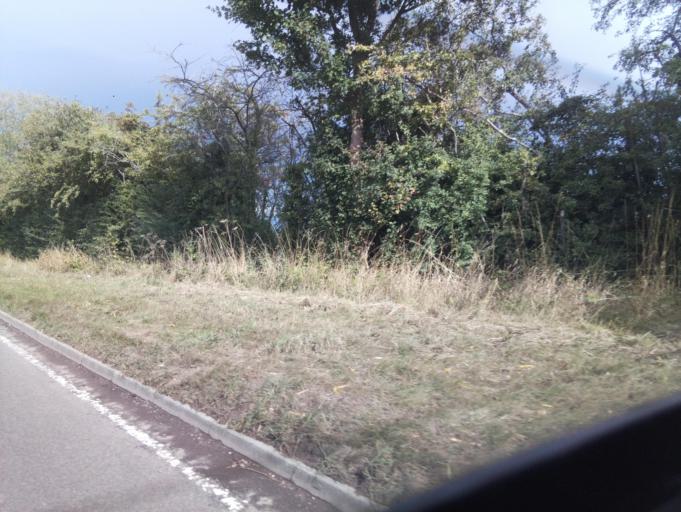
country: GB
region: England
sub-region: Shropshire
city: Shifnal
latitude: 52.6528
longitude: -2.3983
